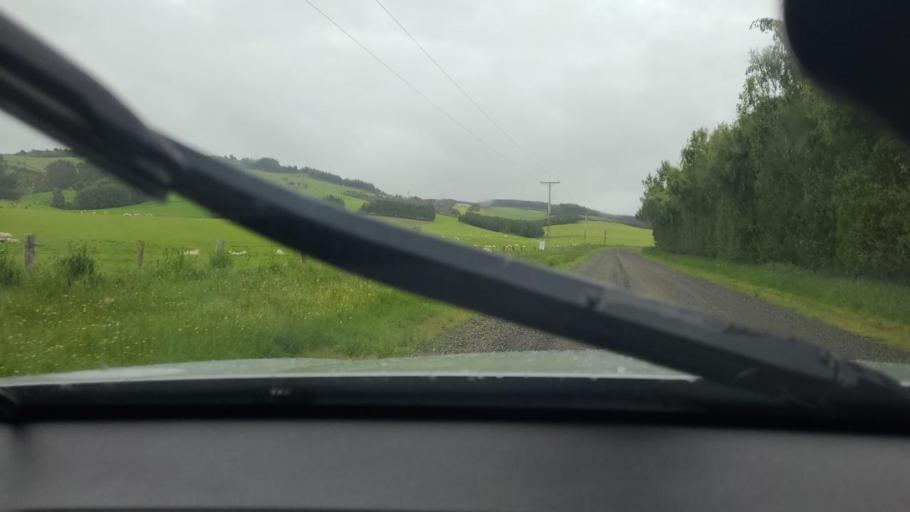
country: NZ
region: Southland
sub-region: Southland District
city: Riverton
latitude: -46.1660
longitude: 168.0022
